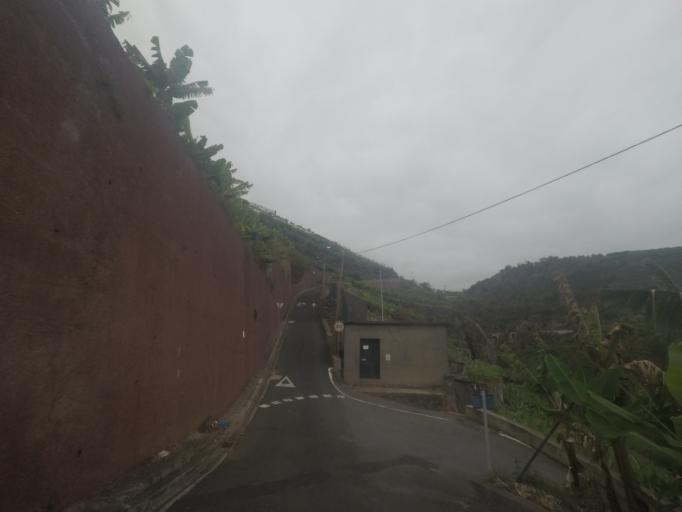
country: PT
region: Madeira
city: Camara de Lobos
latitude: 32.6577
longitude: -16.9648
